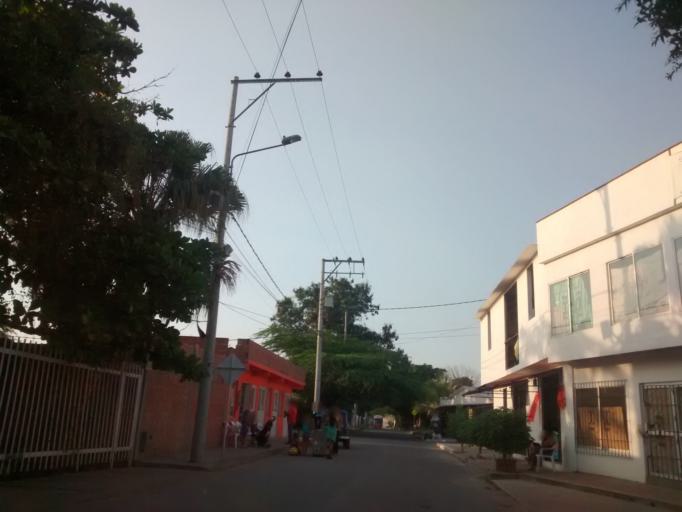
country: CO
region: Cundinamarca
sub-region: Girardot
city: Girardot City
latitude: 4.3180
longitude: -74.7839
